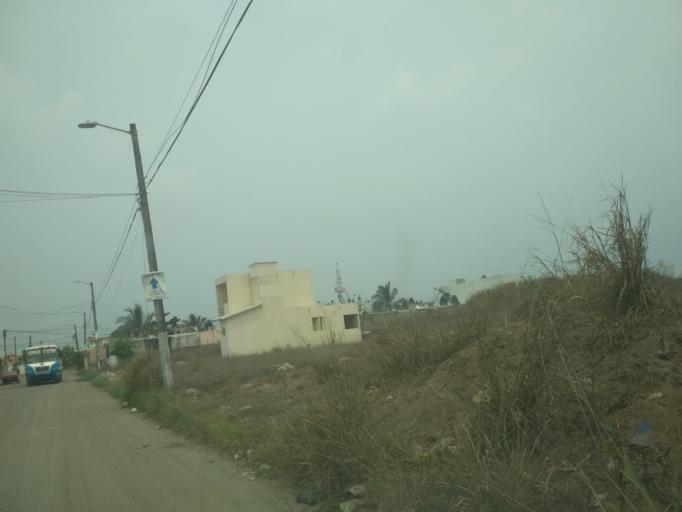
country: MX
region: Veracruz
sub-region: Veracruz
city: Arboledas
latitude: 19.2069
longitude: -96.2137
